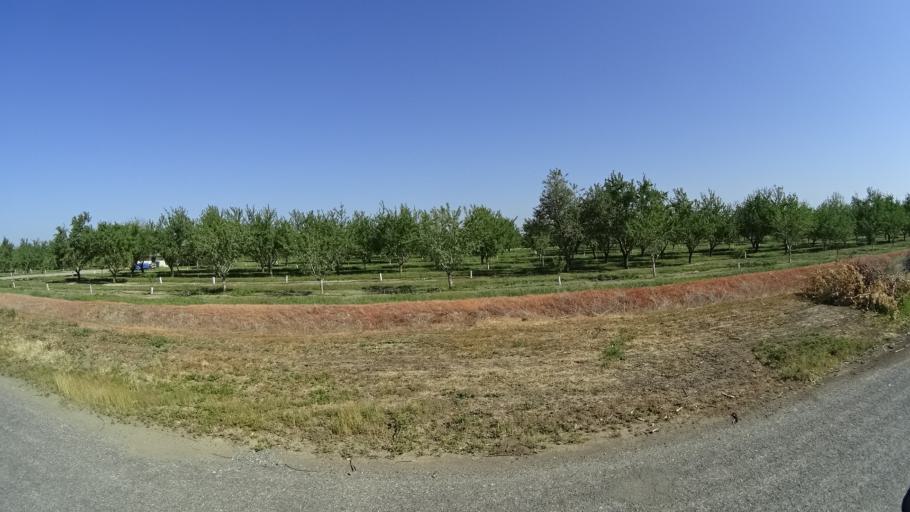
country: US
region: California
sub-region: Glenn County
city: Hamilton City
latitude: 39.6451
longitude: -122.0197
